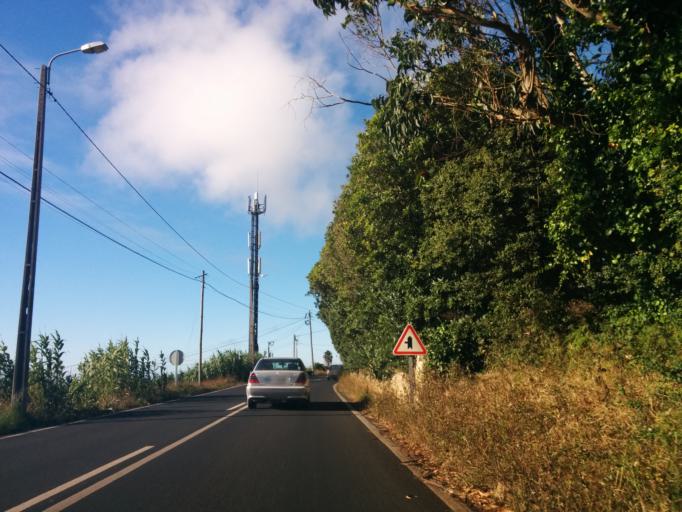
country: PT
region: Lisbon
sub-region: Sintra
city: Colares
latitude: 38.7789
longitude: -9.4761
